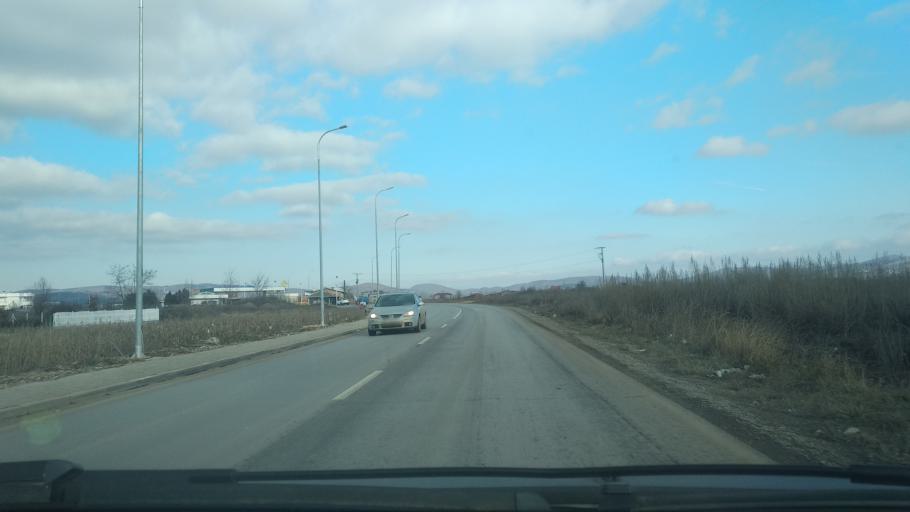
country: XK
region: Pristina
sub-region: Komuna e Obiliqit
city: Obiliq
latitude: 42.7195
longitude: 21.0955
